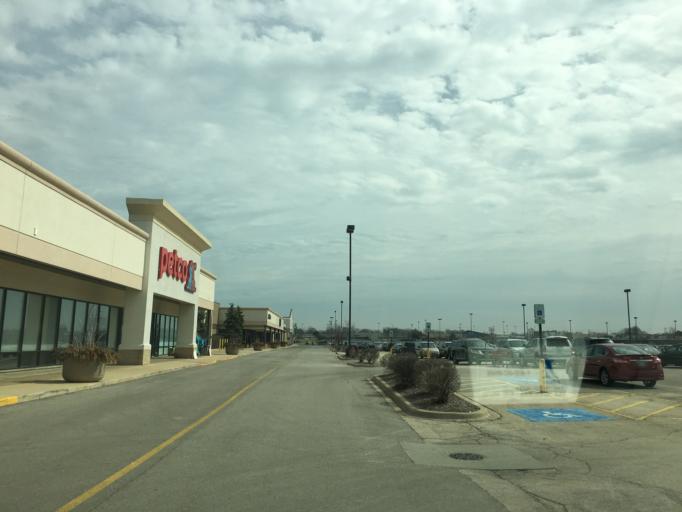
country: US
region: Illinois
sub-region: DuPage County
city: Woodridge
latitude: 41.7537
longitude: -88.0181
